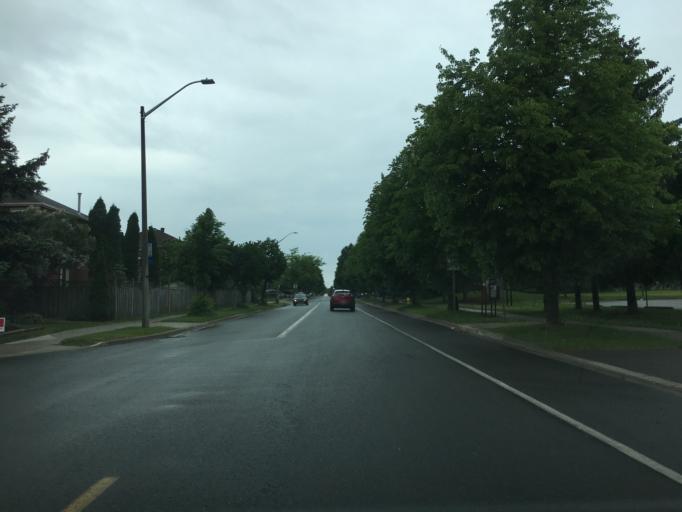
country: CA
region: Ontario
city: Markham
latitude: 43.8374
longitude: -79.2612
